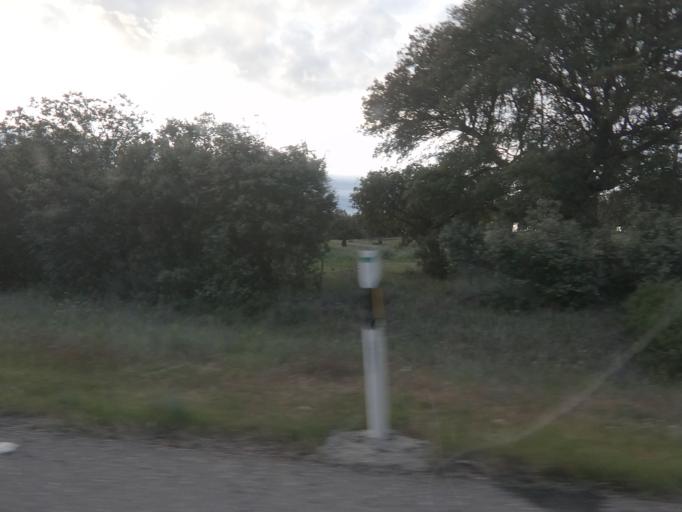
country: ES
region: Extremadura
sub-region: Provincia de Badajoz
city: La Roca de la Sierra
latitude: 39.1383
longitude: -6.6568
